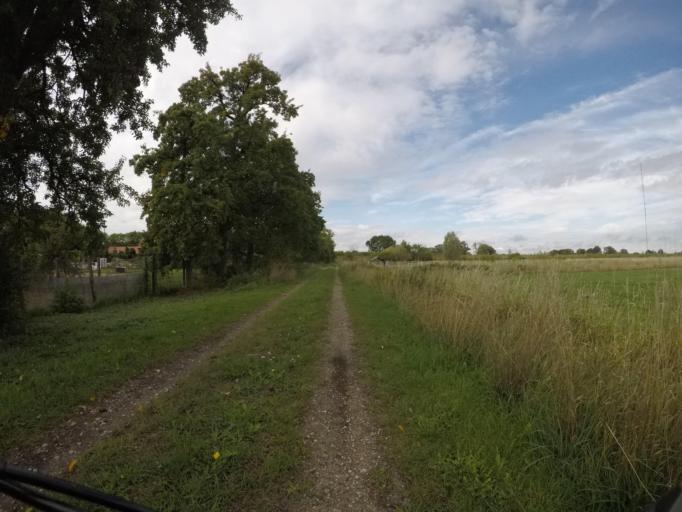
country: DE
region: Lower Saxony
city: Tosterglope
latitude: 53.2602
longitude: 10.8338
